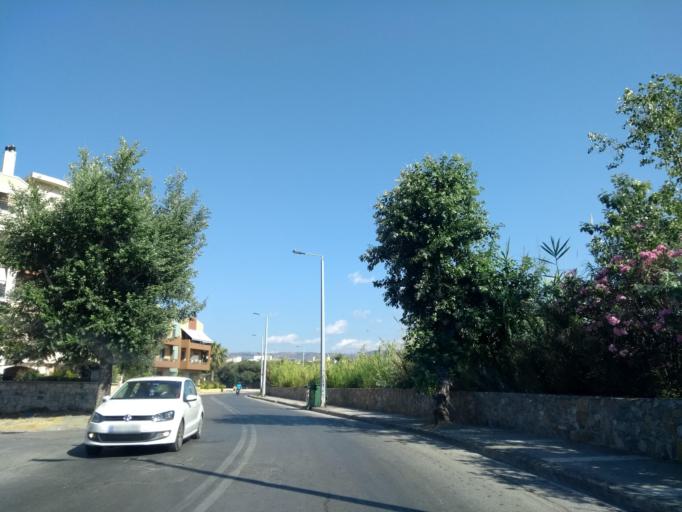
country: GR
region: Crete
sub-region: Nomos Chanias
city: Perivolia
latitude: 35.5091
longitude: 24.0029
